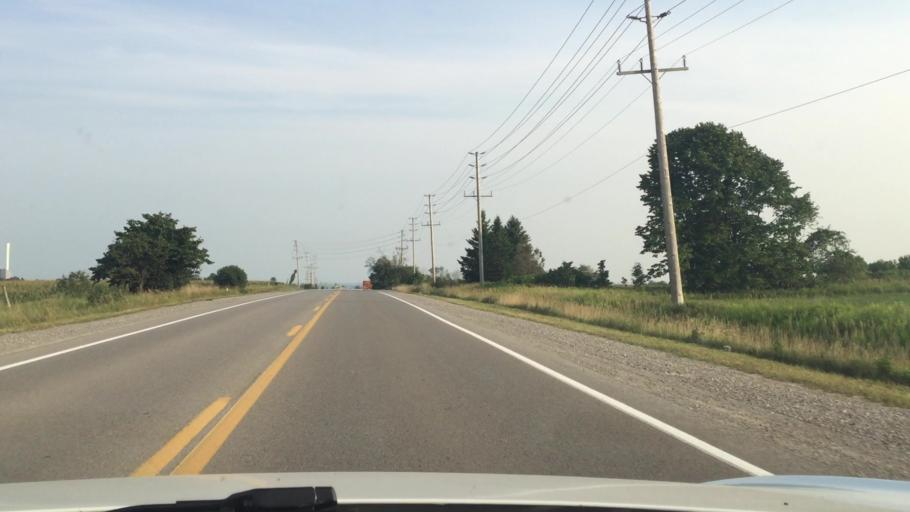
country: CA
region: Ontario
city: Oshawa
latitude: 43.8889
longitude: -78.7680
